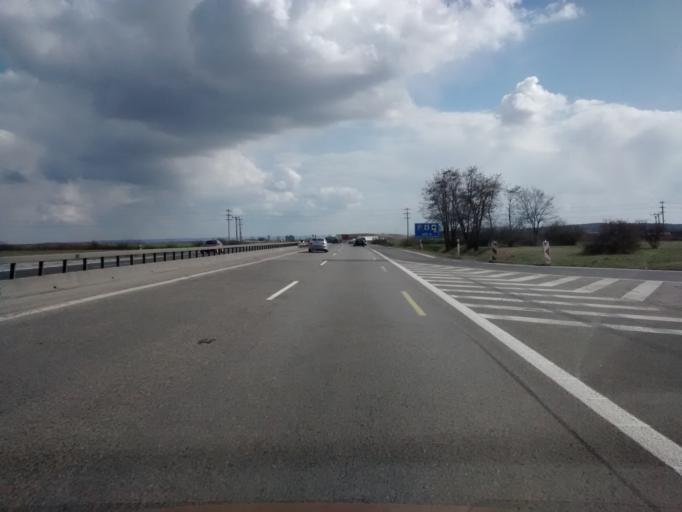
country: CZ
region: Central Bohemia
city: Zdiby
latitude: 50.1761
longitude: 14.4526
